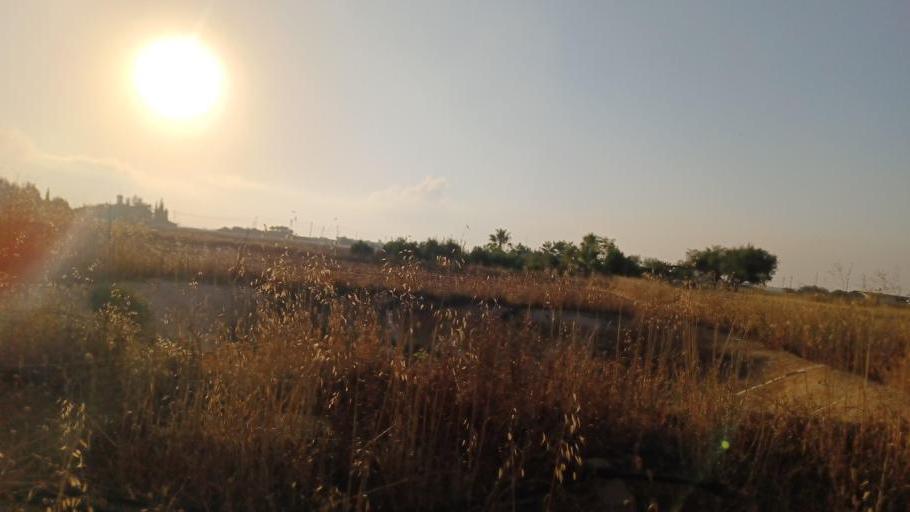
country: CY
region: Ammochostos
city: Avgorou
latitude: 35.0331
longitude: 33.8620
